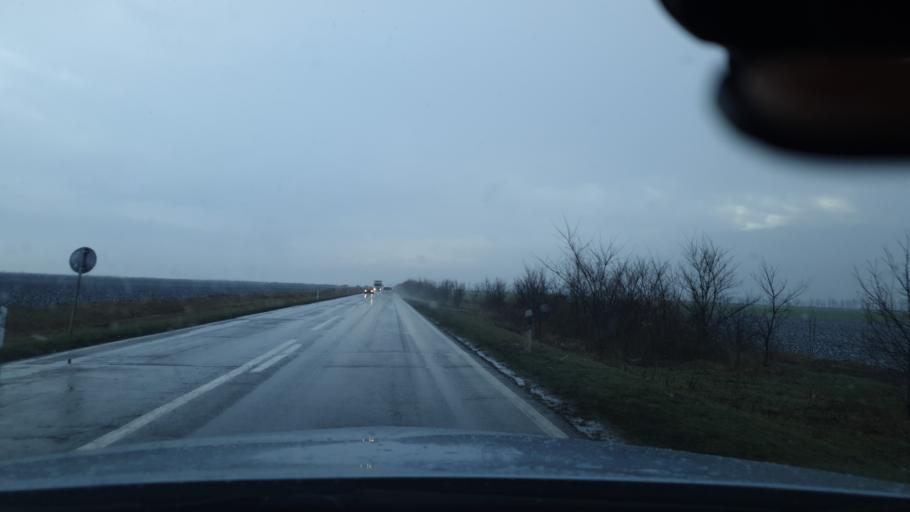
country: RS
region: Autonomna Pokrajina Vojvodina
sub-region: Juznobanatski Okrug
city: Pancevo
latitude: 44.8488
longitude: 20.7765
